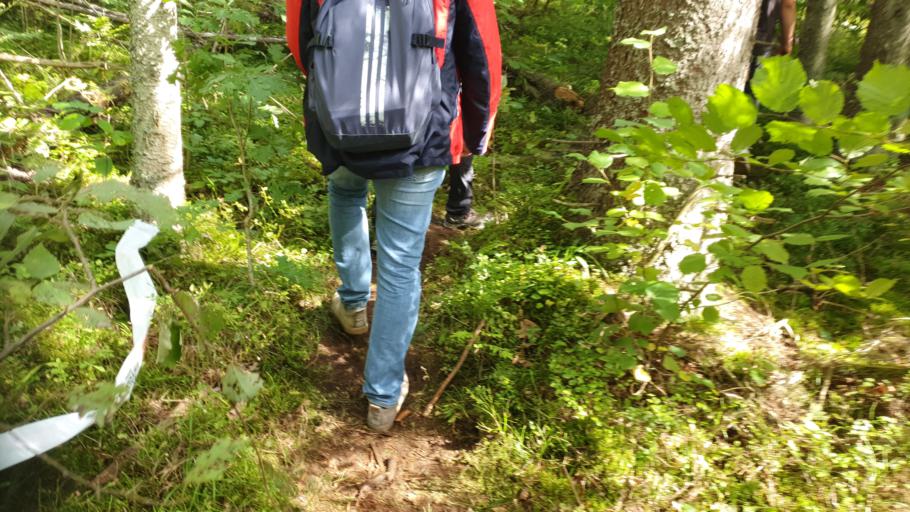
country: EE
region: Tartu
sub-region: UElenurme vald
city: Ulenurme
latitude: 58.1318
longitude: 26.7733
